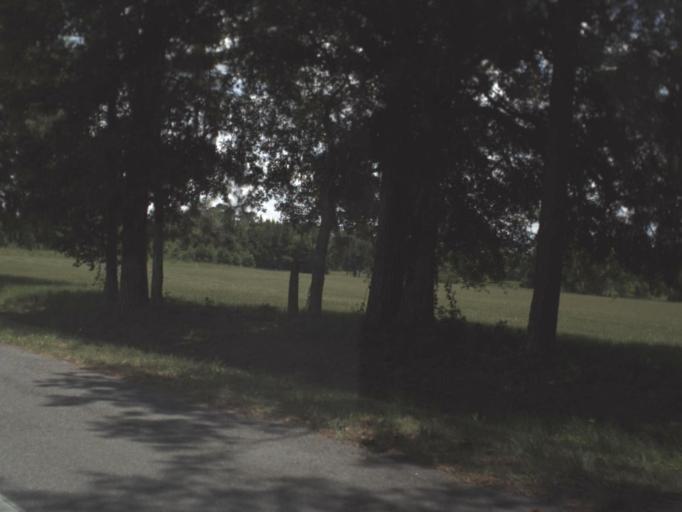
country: US
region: Florida
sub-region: Union County
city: Lake Butler
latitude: 30.0023
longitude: -82.5054
